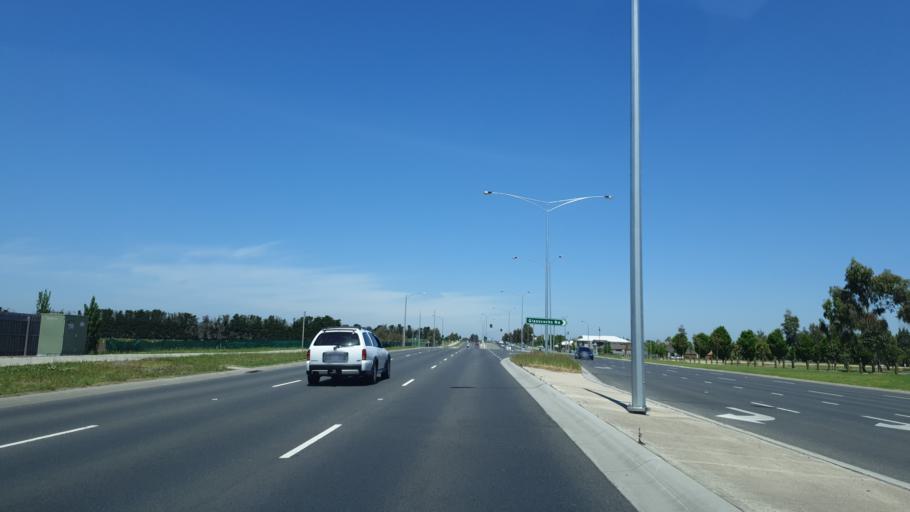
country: AU
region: Victoria
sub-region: Casey
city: Cranbourne North
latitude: -38.0695
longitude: 145.2983
